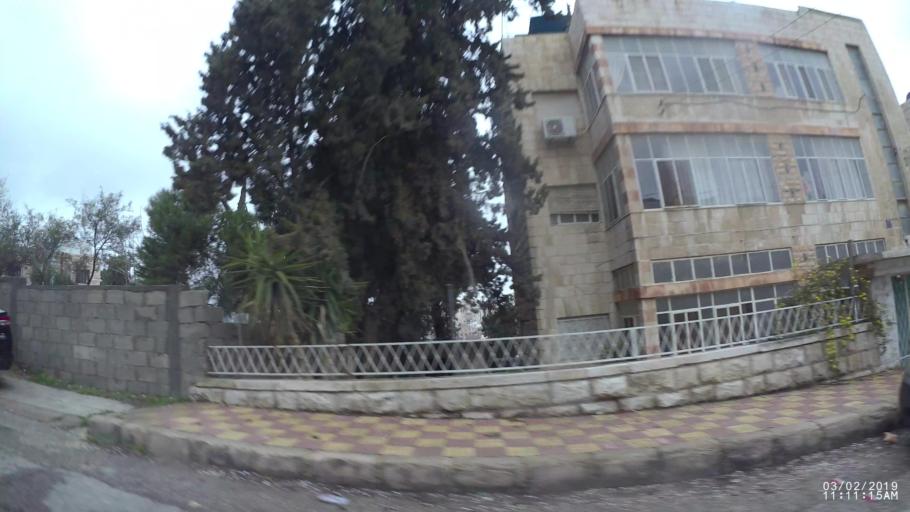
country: JO
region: Amman
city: Amman
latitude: 31.9526
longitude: 35.9209
